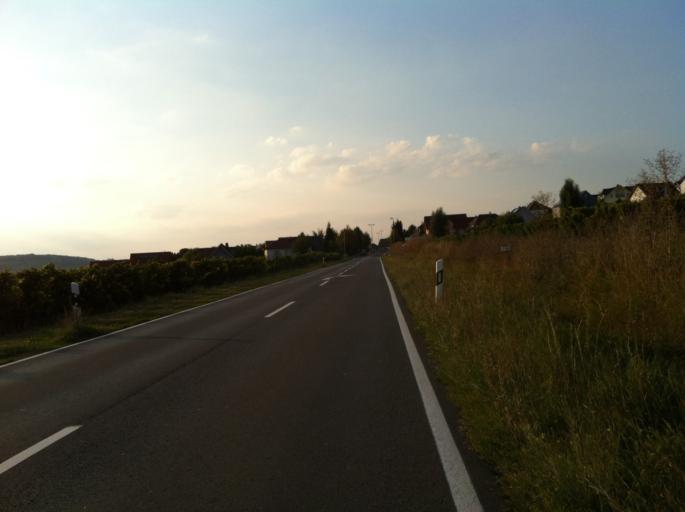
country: DE
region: Rheinland-Pfalz
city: Schwabenheim
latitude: 49.9248
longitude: 8.1027
